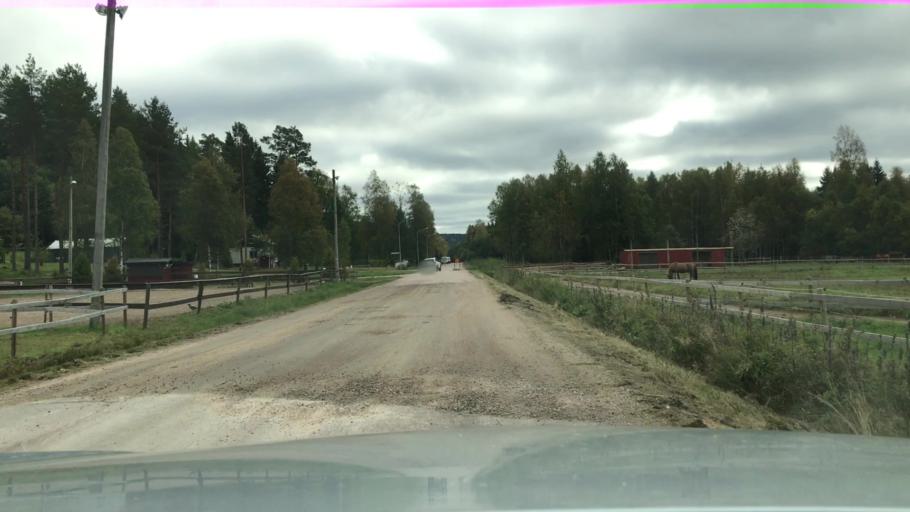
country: SE
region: Vaermland
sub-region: Munkfors Kommun
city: Munkfors
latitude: 59.8383
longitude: 13.5045
